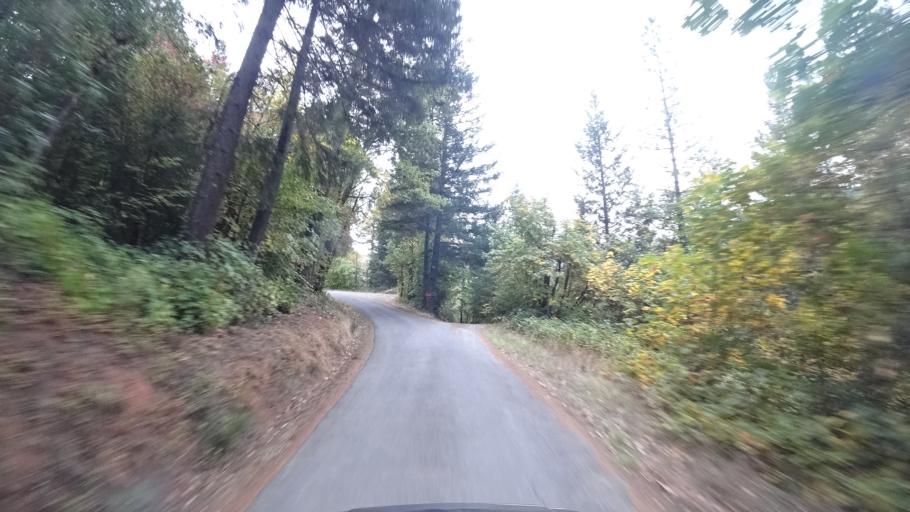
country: US
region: California
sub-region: Siskiyou County
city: Happy Camp
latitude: 41.7940
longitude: -123.3434
